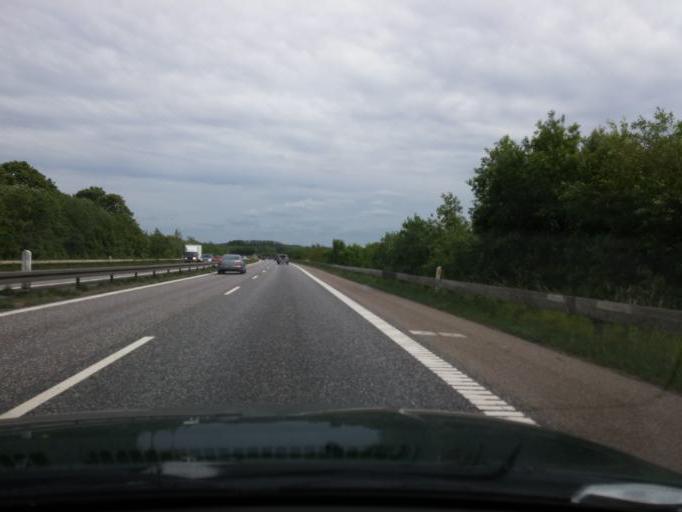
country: DK
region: South Denmark
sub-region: Odense Kommune
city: Bellinge
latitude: 55.3698
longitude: 10.3067
